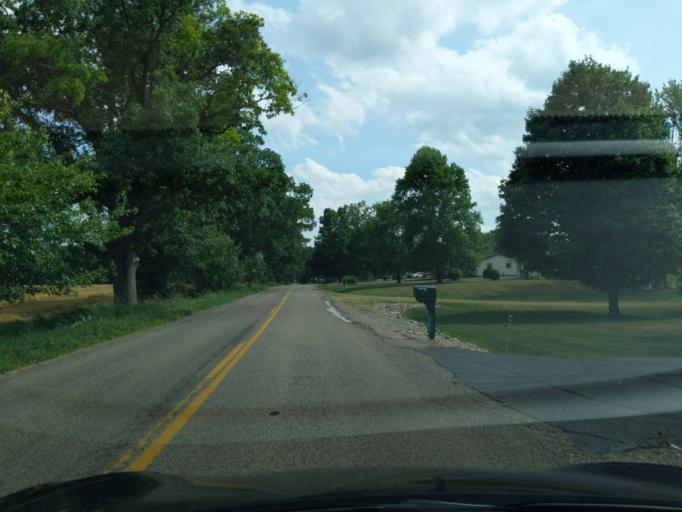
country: US
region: Michigan
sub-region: Eaton County
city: Eaton Rapids
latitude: 42.5040
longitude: -84.6307
